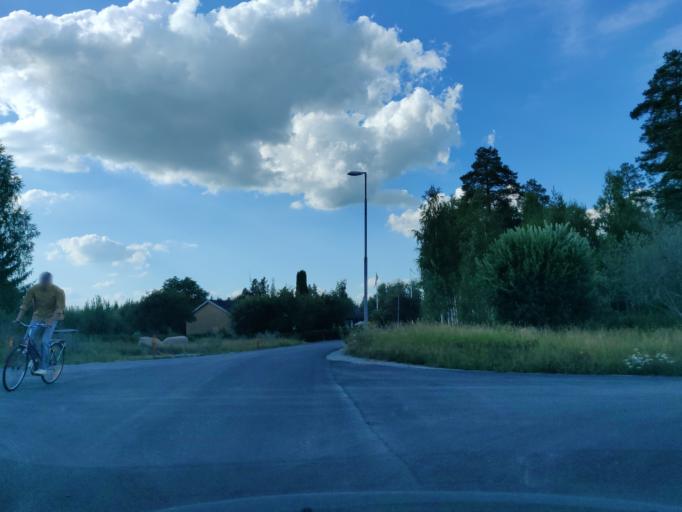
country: SE
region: Vaermland
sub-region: Hagfors Kommun
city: Hagfors
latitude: 60.0189
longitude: 13.6773
